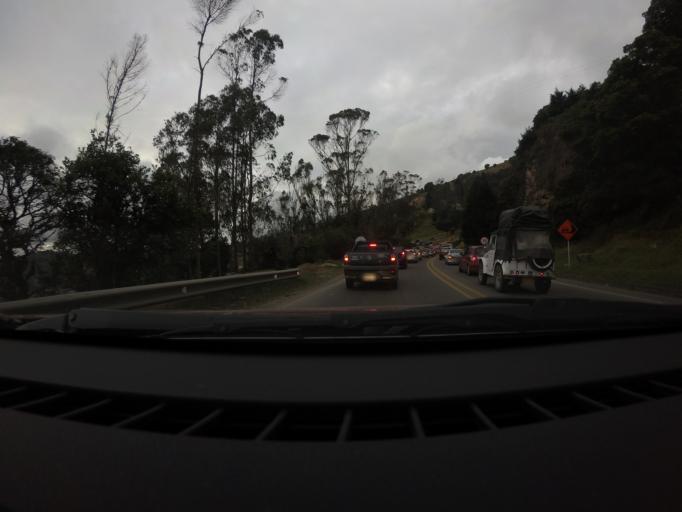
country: CO
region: Boyaca
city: Samaca
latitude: 5.4597
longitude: -73.4179
